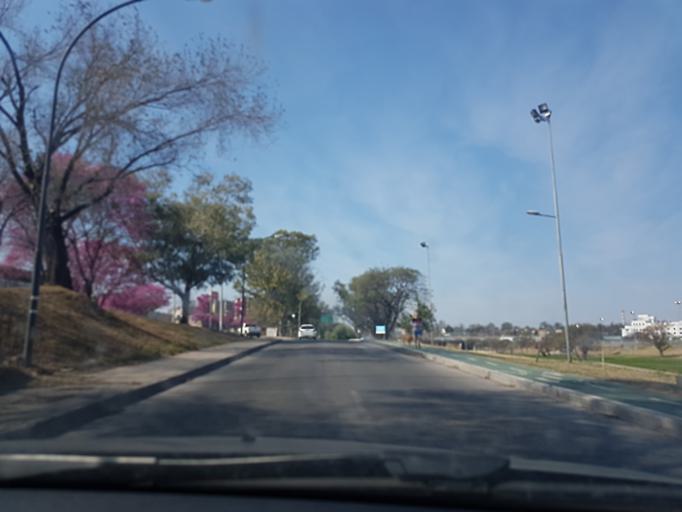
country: AR
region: Cordoba
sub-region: Departamento de Capital
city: Cordoba
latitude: -31.4181
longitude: -64.1726
